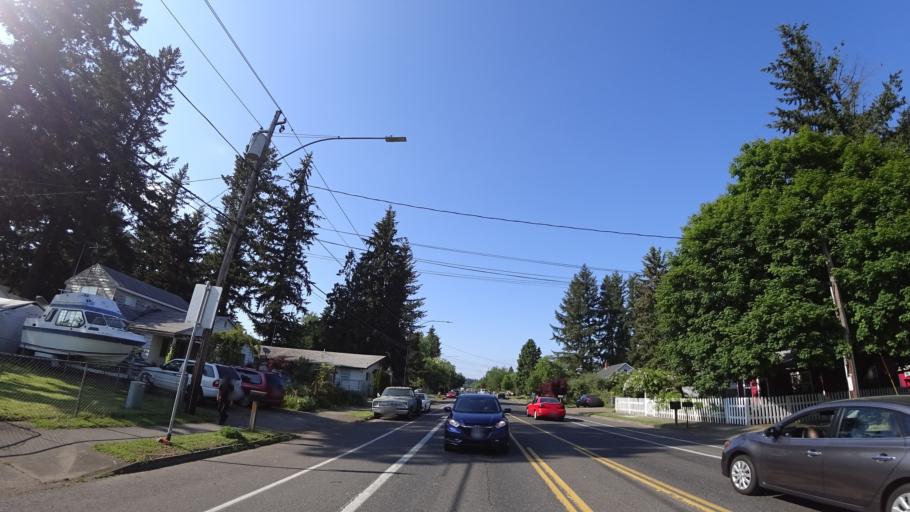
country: US
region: Oregon
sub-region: Multnomah County
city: Lents
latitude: 45.5112
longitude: -122.5108
